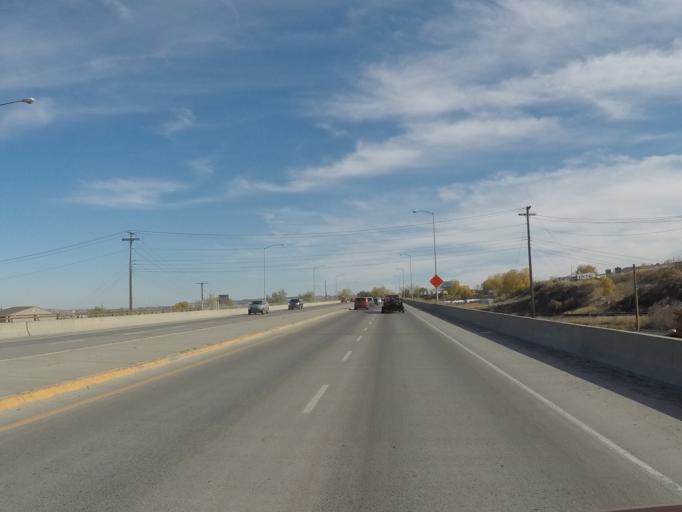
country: US
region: Montana
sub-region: Yellowstone County
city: Billings
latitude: 45.7964
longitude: -108.4695
